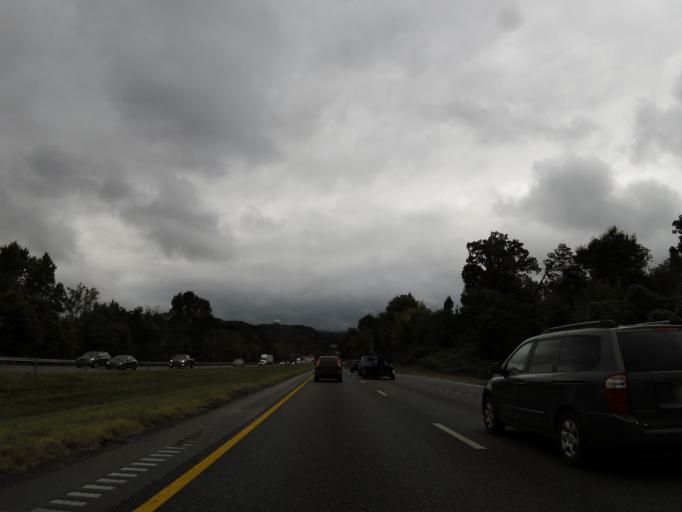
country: US
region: Tennessee
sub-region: Hamilton County
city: Lookout Mountain
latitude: 35.0264
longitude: -85.3695
